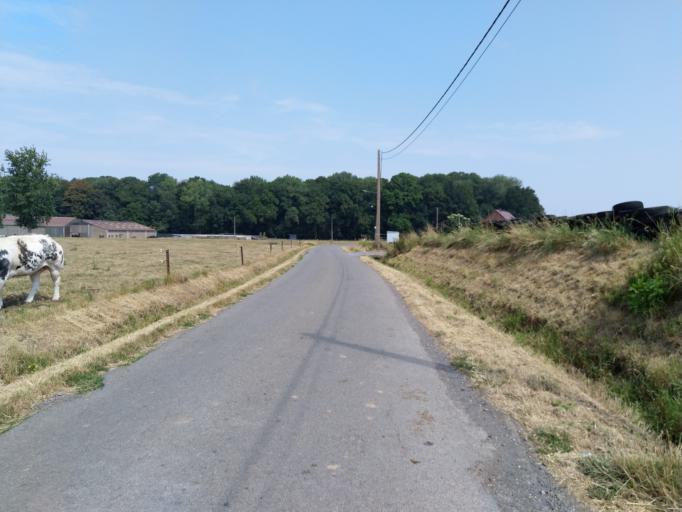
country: BE
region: Wallonia
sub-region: Province du Hainaut
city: Roeulx
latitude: 50.5092
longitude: 4.0523
